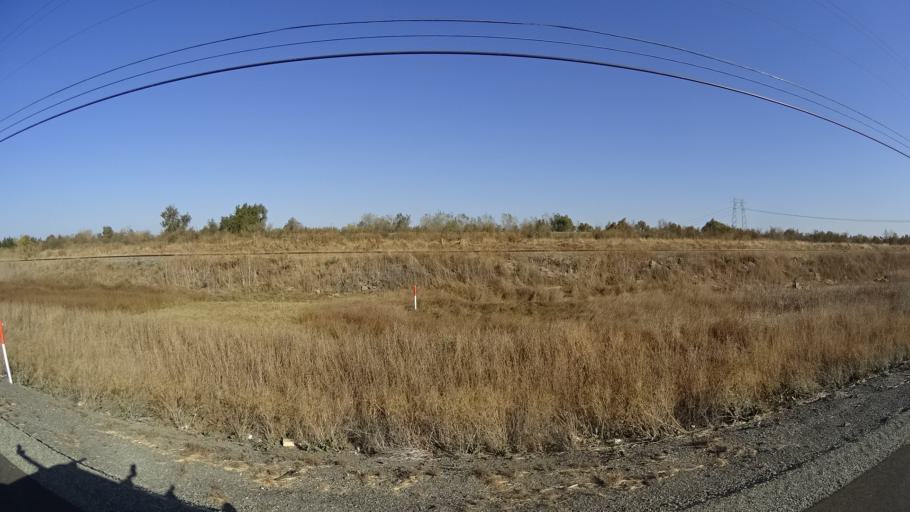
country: US
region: California
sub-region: Yolo County
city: Woodland
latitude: 38.6767
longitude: -121.6785
